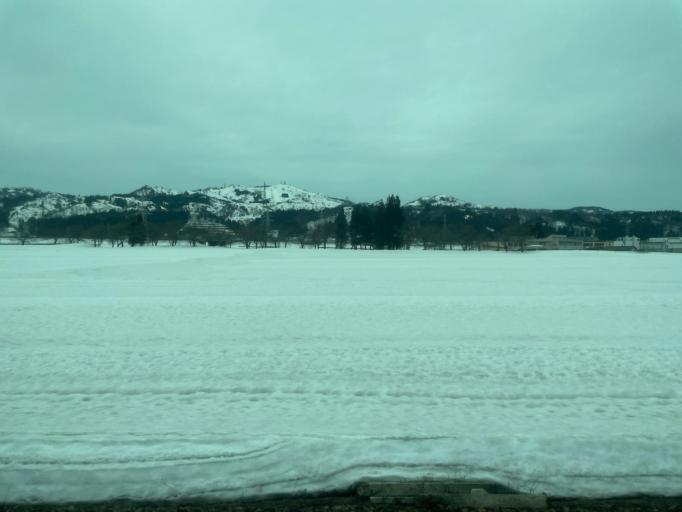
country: JP
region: Niigata
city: Muikamachi
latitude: 37.0529
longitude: 138.8664
